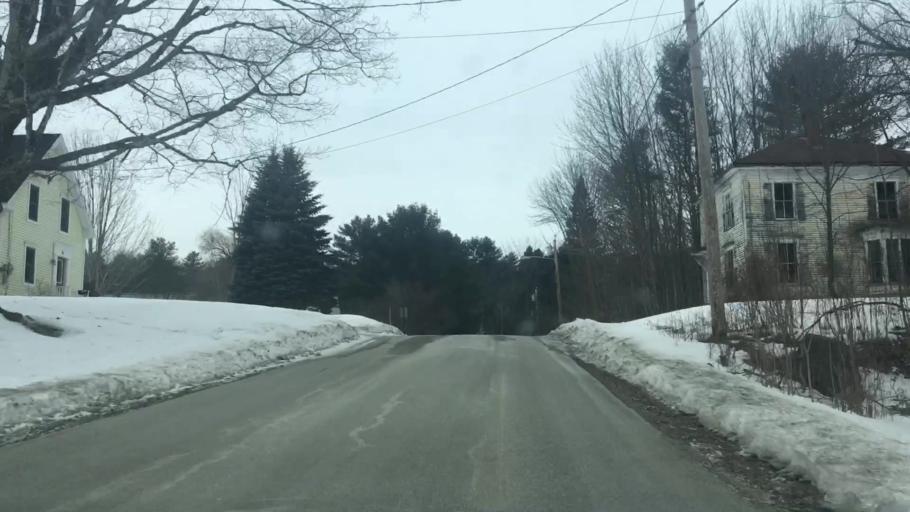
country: US
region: Maine
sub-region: Kennebec County
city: Winthrop
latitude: 44.3069
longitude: -69.9815
